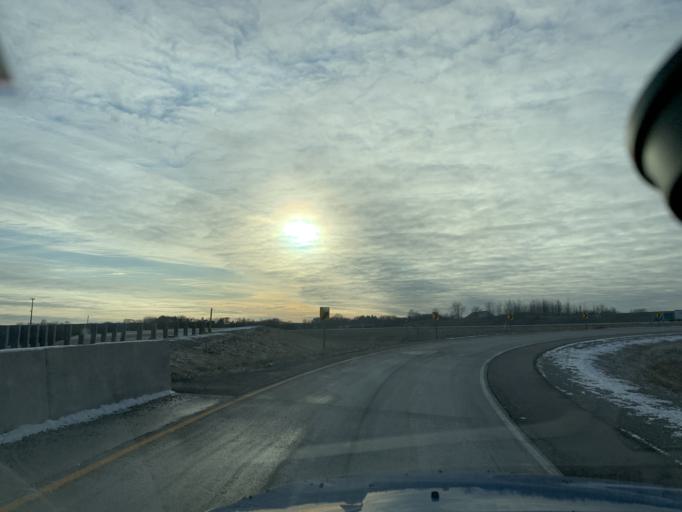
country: US
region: Wisconsin
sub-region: Rock County
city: Edgerton
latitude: 42.9187
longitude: -89.0833
